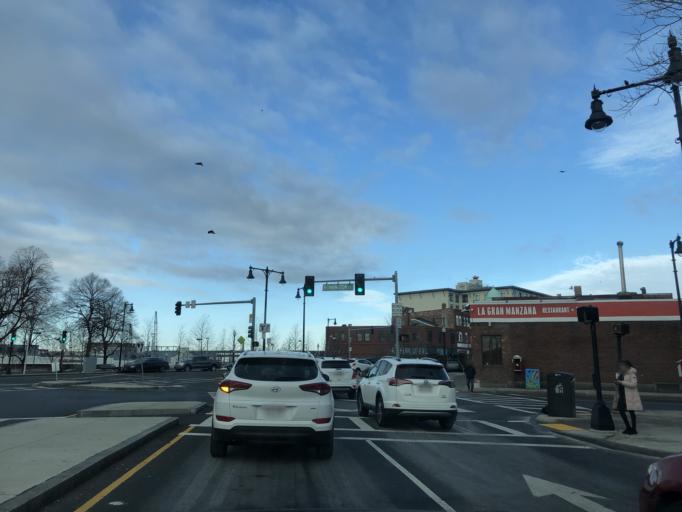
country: US
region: Massachusetts
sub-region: Suffolk County
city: Chelsea
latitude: 42.3748
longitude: -71.0385
